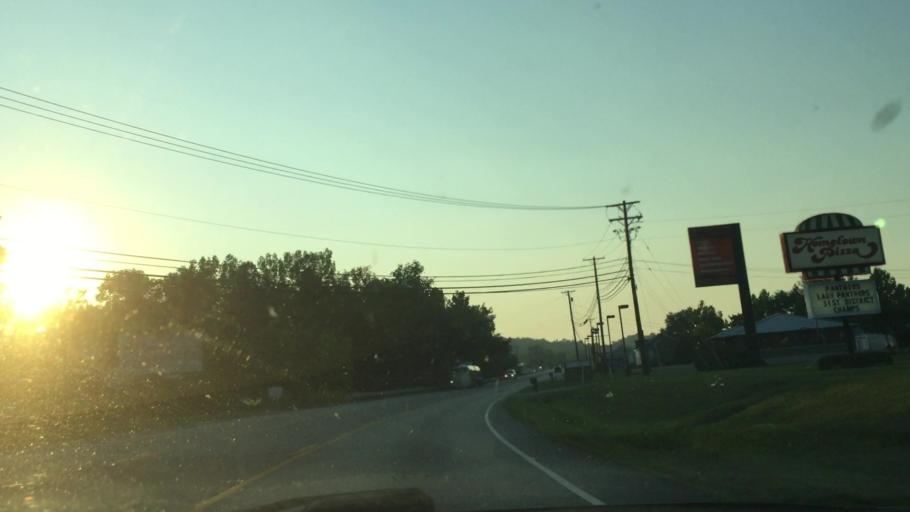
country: US
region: Kentucky
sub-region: Carroll County
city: Carrollton
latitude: 38.6585
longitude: -85.1363
